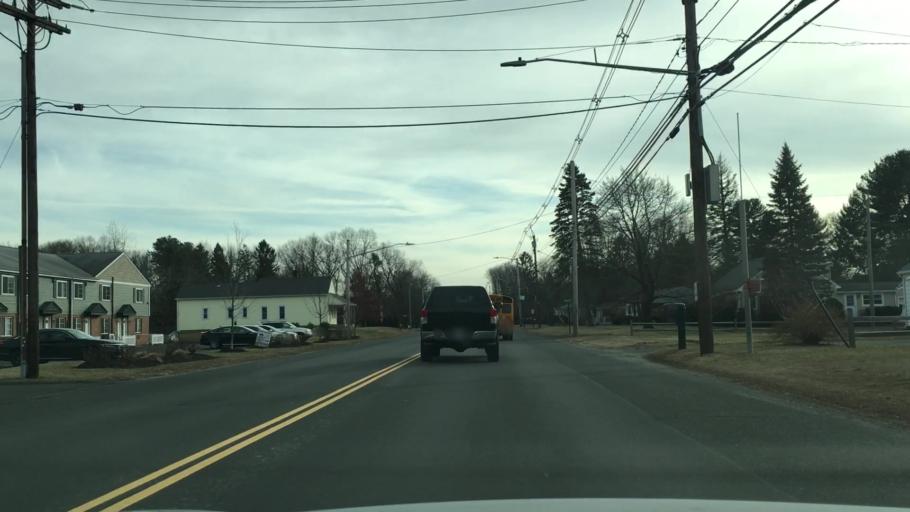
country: US
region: Massachusetts
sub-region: Hampden County
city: Westfield
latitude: 42.1040
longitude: -72.7645
